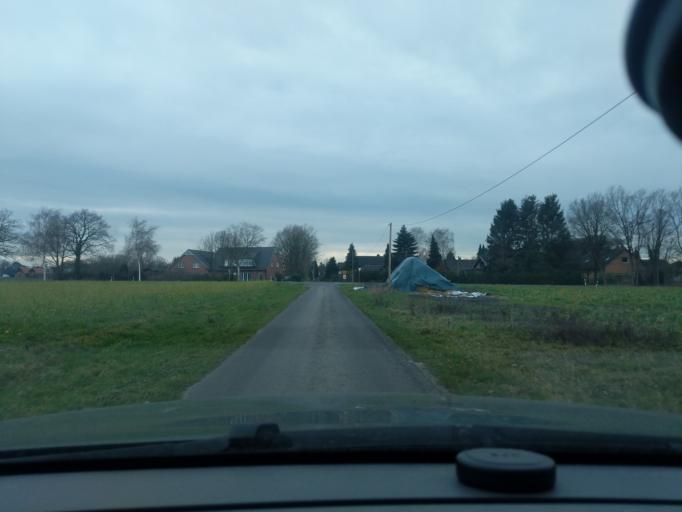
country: DE
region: Lower Saxony
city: Hemslingen
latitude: 53.0946
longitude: 9.6056
